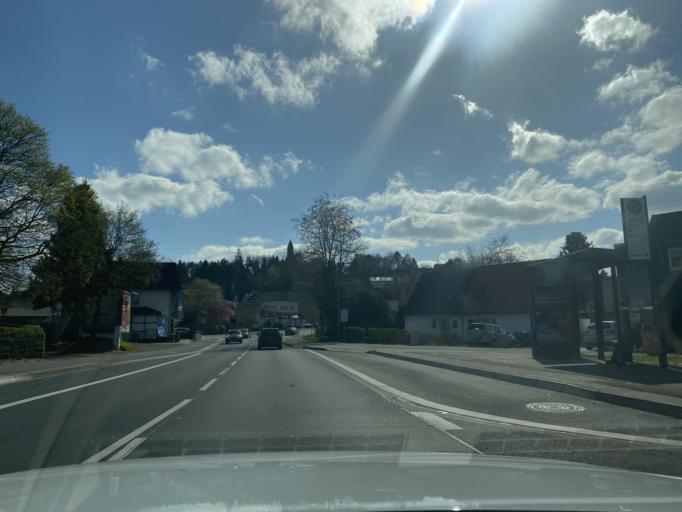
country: DE
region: North Rhine-Westphalia
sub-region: Regierungsbezirk Koln
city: Bergisch Gladbach
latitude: 50.9707
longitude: 7.1496
